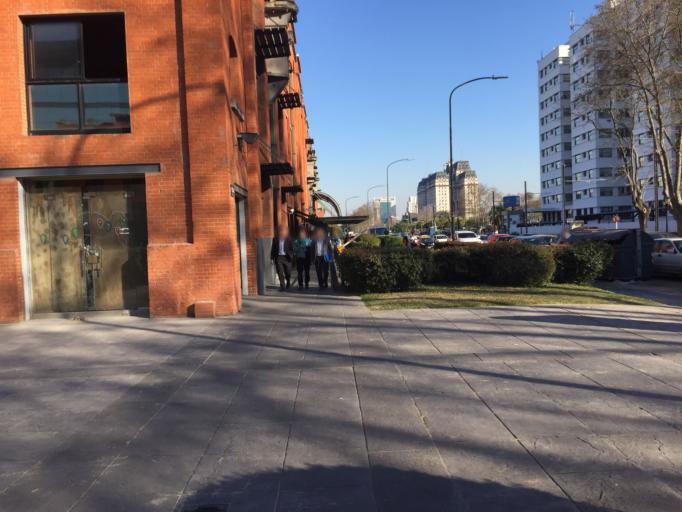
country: AR
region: Buenos Aires F.D.
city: Buenos Aires
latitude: -34.6035
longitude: -58.3671
